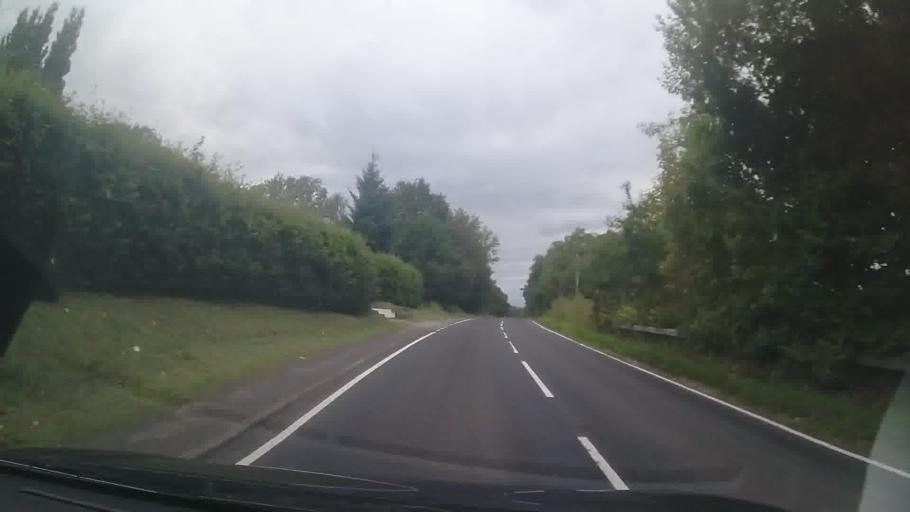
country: GB
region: Scotland
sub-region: Argyll and Bute
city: Garelochhead
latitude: 56.2216
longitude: -5.0338
